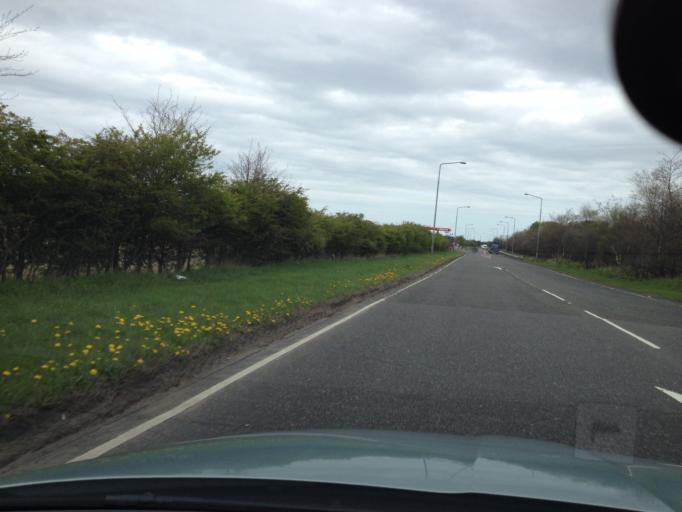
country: GB
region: Scotland
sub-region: West Lothian
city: Livingston
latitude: 55.9090
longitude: -3.5748
